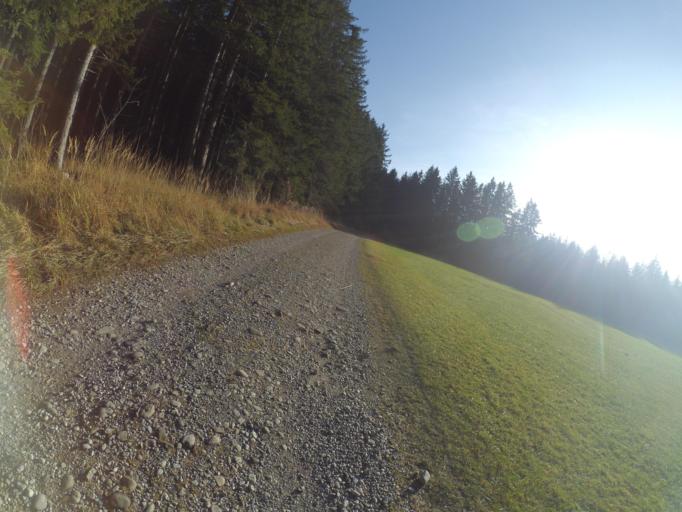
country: DE
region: Bavaria
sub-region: Swabia
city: Ruderatshofen
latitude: 47.8044
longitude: 10.5626
